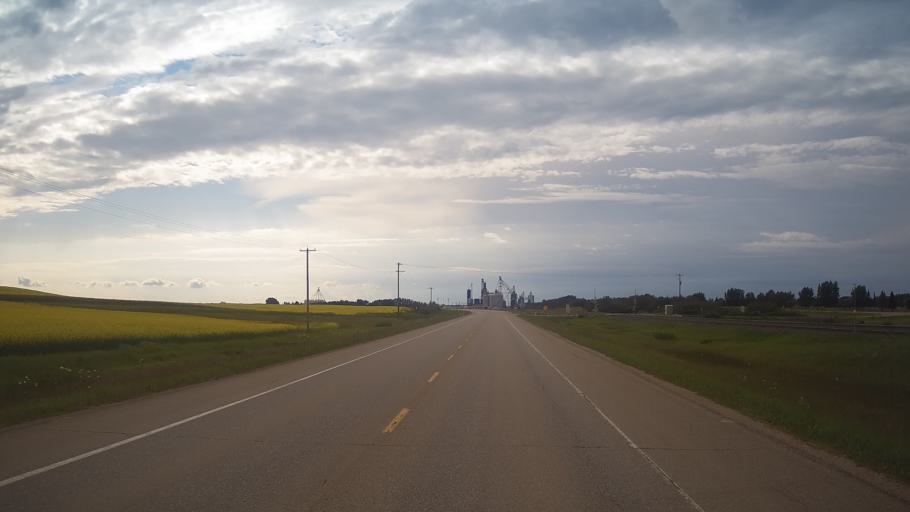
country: CA
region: Alberta
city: Viking
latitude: 53.0859
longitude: -111.7574
